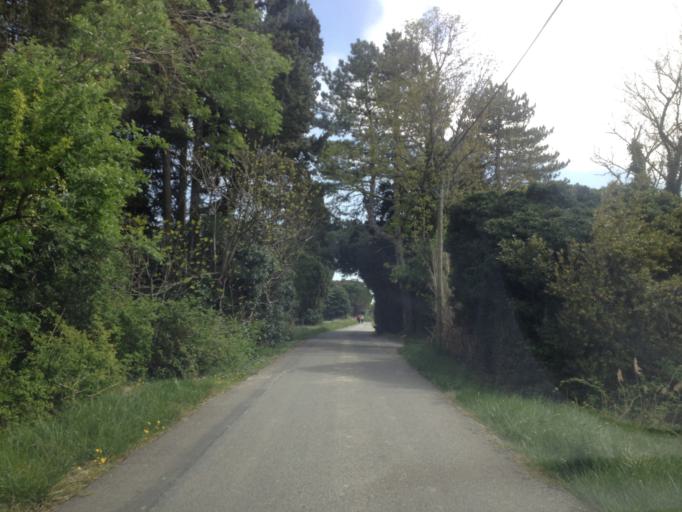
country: FR
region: Provence-Alpes-Cote d'Azur
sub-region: Departement du Vaucluse
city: Caderousse
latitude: 44.1140
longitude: 4.7827
